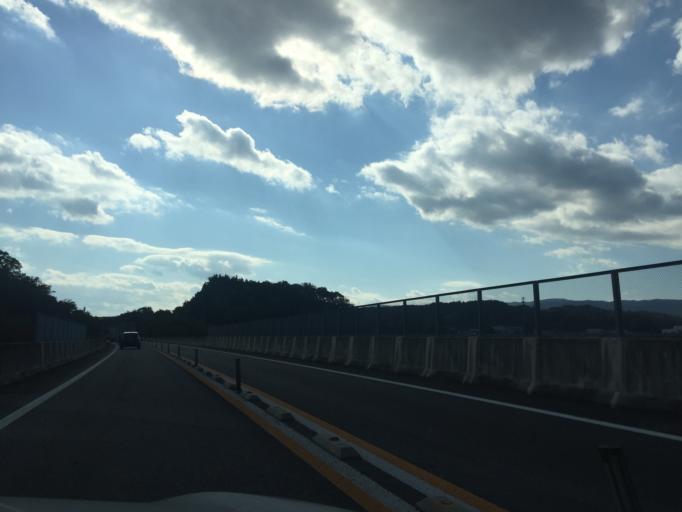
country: JP
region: Fukushima
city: Iwaki
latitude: 37.0900
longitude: 140.8434
